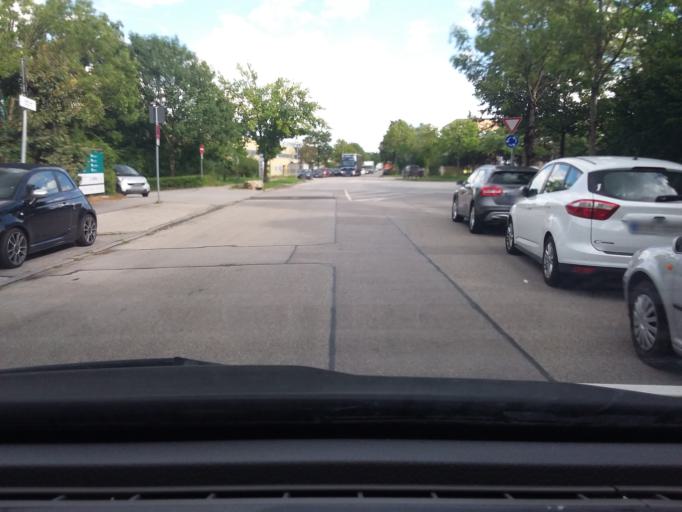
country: DE
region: Bavaria
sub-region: Upper Bavaria
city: Garching bei Munchen
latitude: 48.2545
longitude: 11.6207
